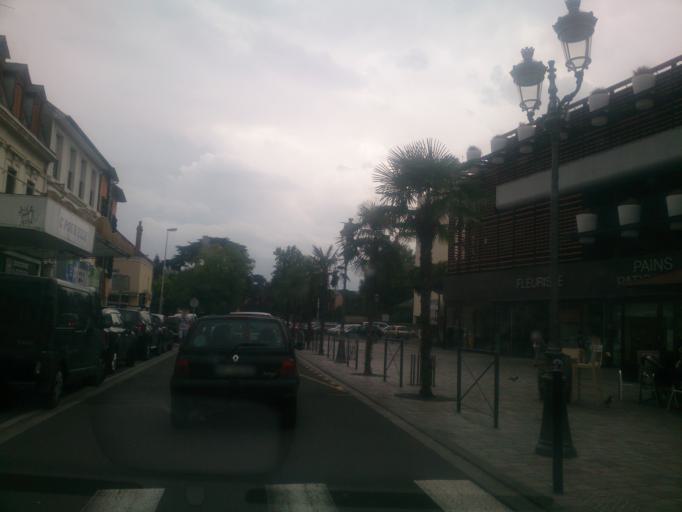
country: FR
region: Midi-Pyrenees
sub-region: Departement des Hautes-Pyrenees
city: Tarbes
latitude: 43.2313
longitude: 0.0751
